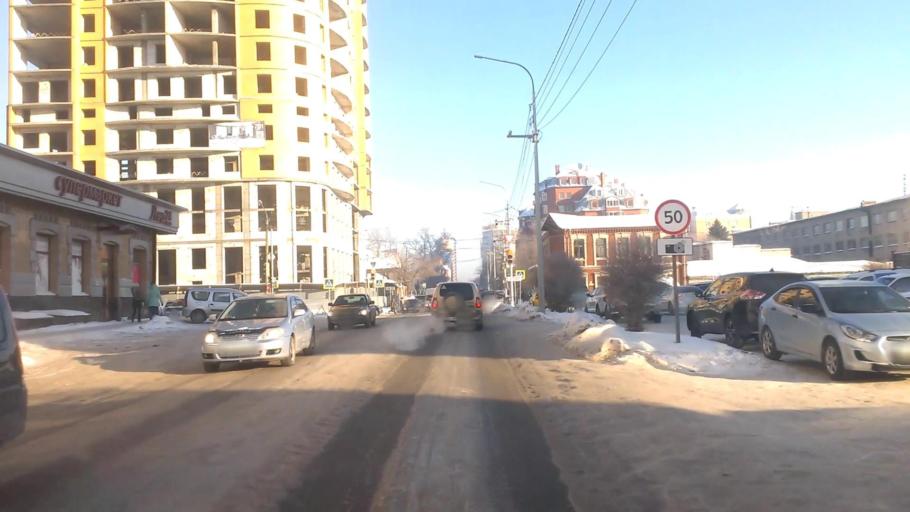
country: RU
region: Altai Krai
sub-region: Gorod Barnaulskiy
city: Barnaul
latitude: 53.3380
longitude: 83.7808
